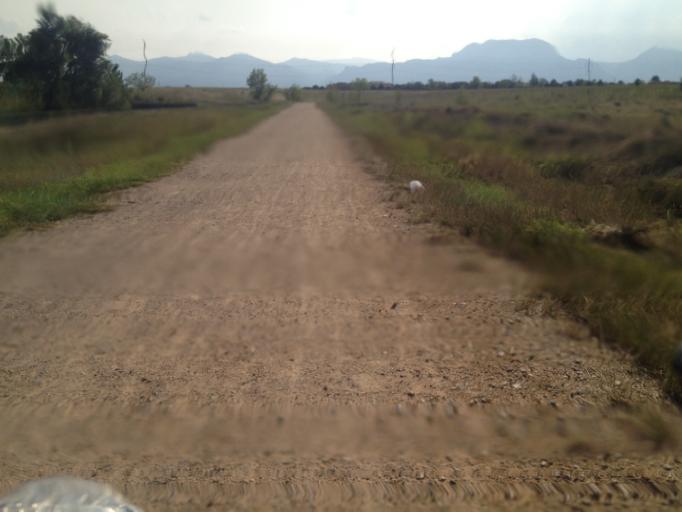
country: US
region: Colorado
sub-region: Boulder County
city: Superior
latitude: 39.9746
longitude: -105.1700
